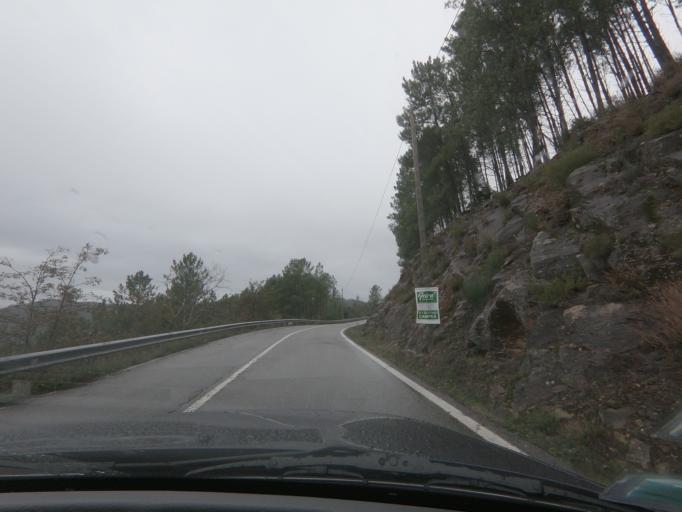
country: PT
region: Vila Real
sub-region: Mondim de Basto
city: Mondim de Basto
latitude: 41.3667
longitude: -7.9246
